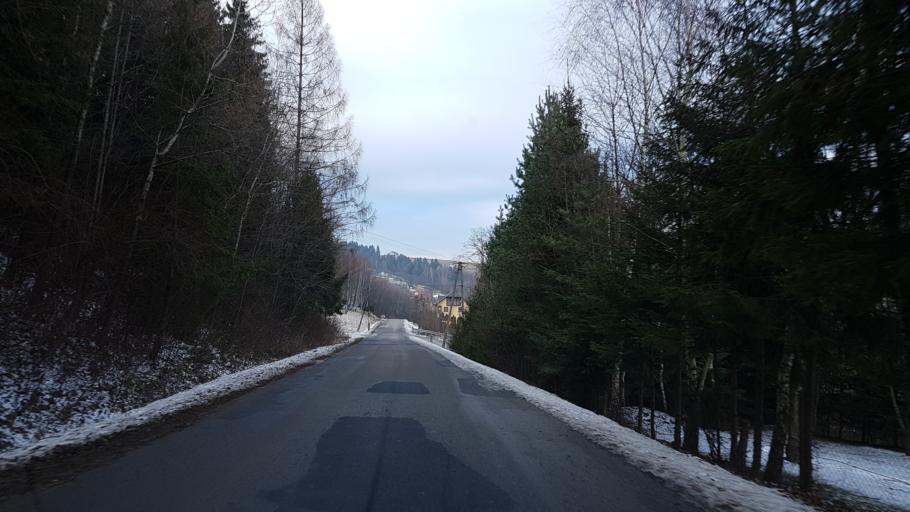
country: PL
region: Lesser Poland Voivodeship
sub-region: Powiat nowosadecki
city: Stary Sacz
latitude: 49.5268
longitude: 20.6077
